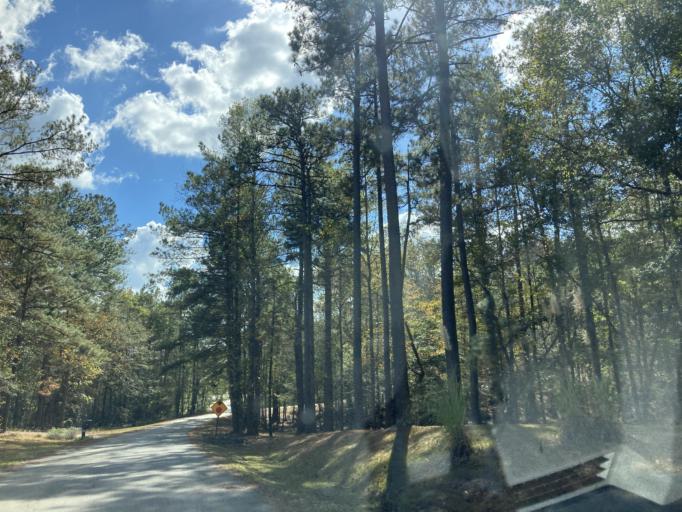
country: US
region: Mississippi
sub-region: Lamar County
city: West Hattiesburg
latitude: 31.2711
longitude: -89.4003
